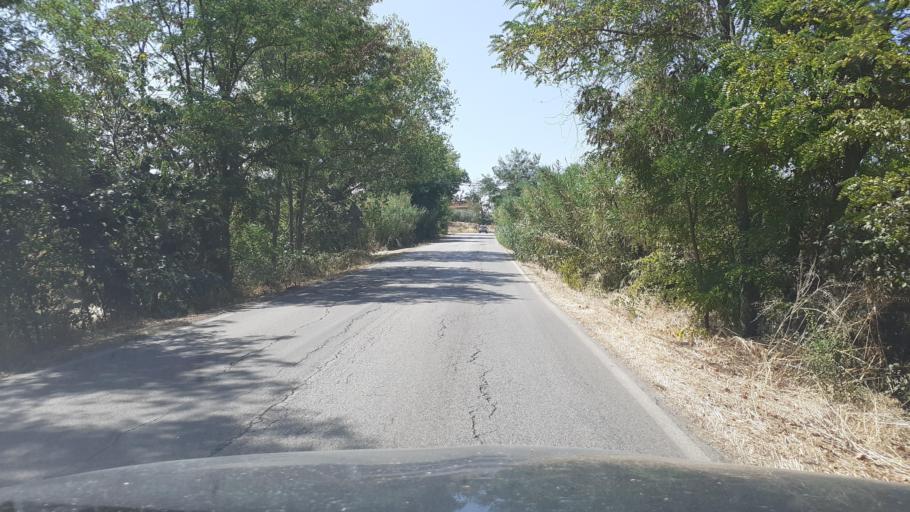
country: IT
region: Abruzzo
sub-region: Provincia di Chieti
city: Santa Maria Imbaro
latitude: 42.2152
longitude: 14.4606
